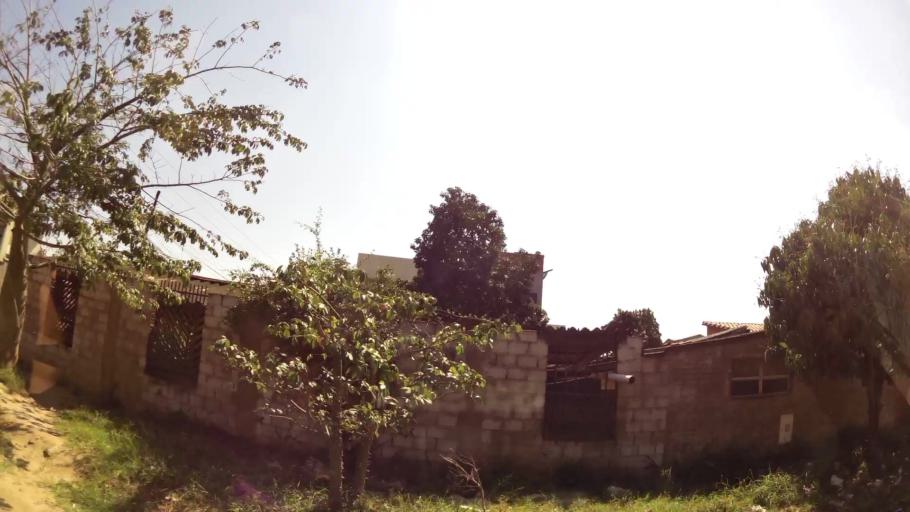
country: BO
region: Santa Cruz
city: Santa Cruz de la Sierra
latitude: -17.7455
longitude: -63.1441
